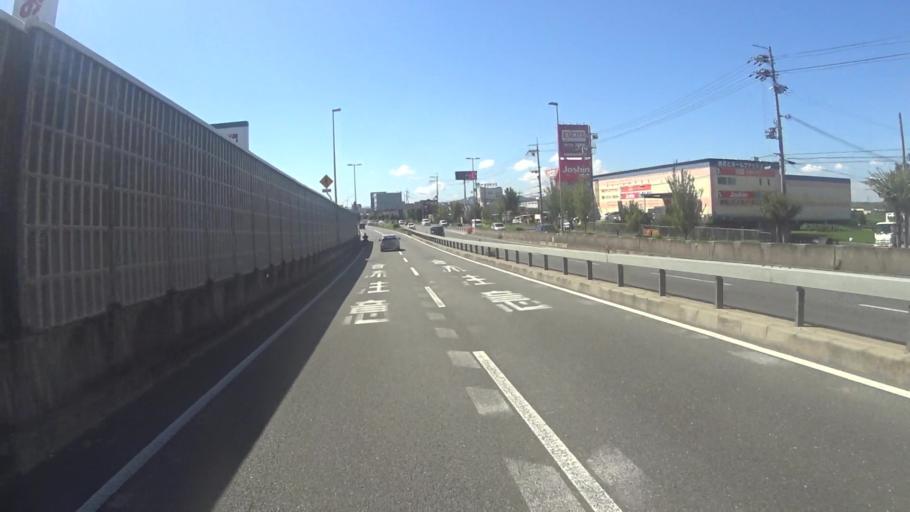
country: JP
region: Kyoto
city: Uji
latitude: 34.8732
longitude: 135.7621
